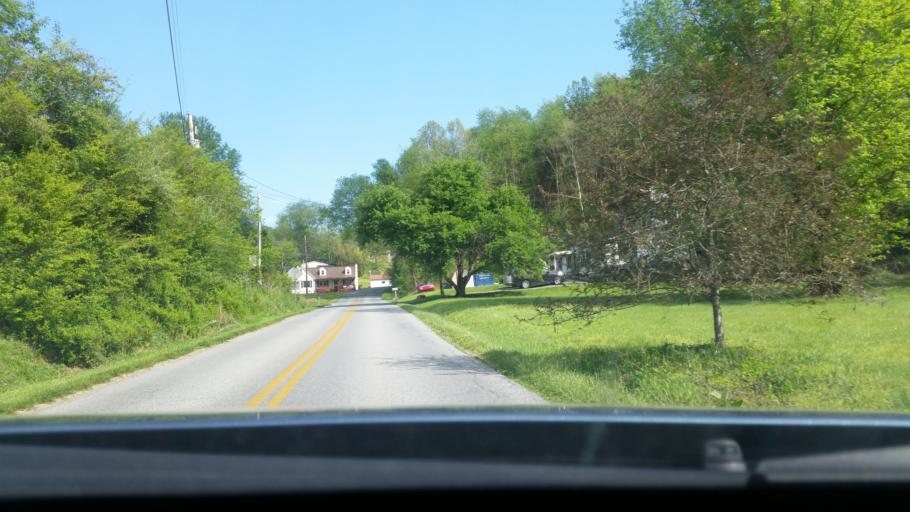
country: US
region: Virginia
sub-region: Giles County
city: Pembroke
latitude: 37.3159
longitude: -80.6343
